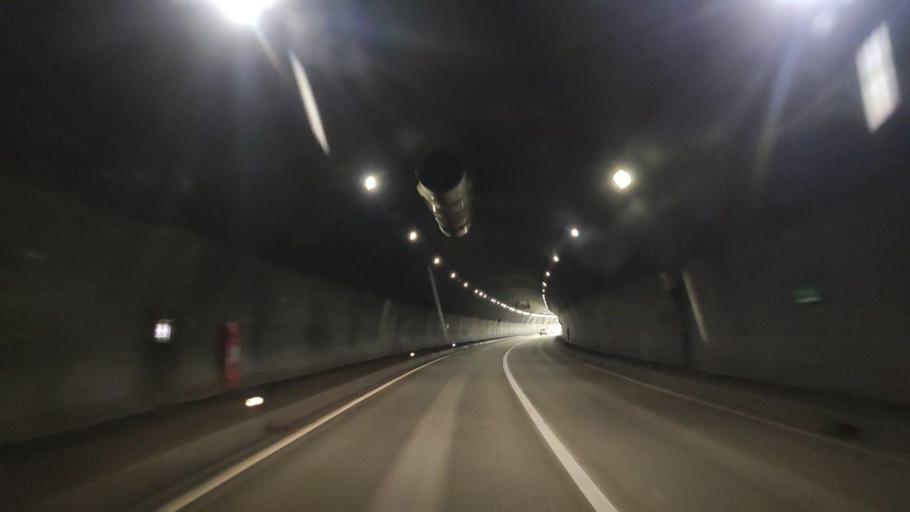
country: JP
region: Nagano
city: Omachi
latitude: 36.5451
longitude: 137.8453
